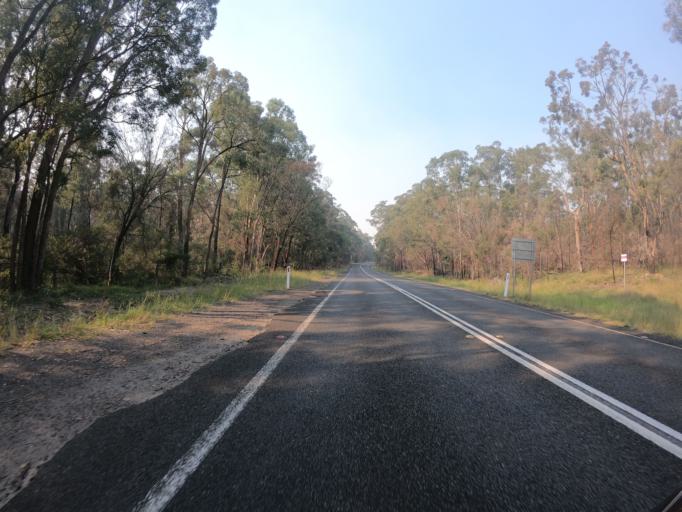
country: AU
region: New South Wales
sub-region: Wollondilly
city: Douglas Park
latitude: -34.2257
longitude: 150.7469
